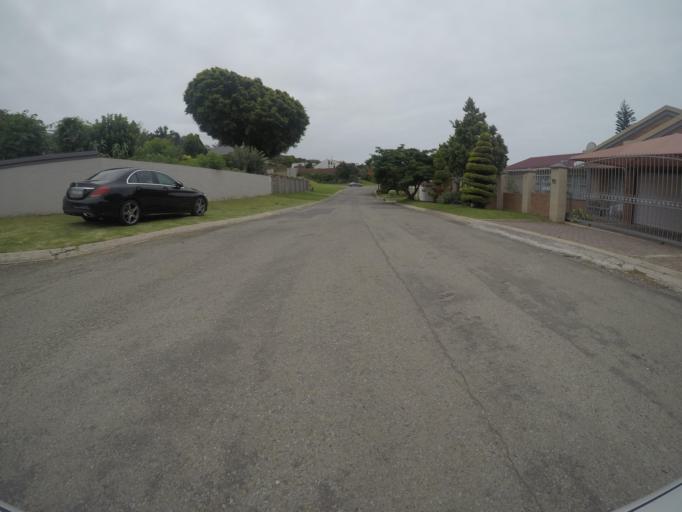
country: ZA
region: Eastern Cape
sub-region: Buffalo City Metropolitan Municipality
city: East London
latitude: -32.9802
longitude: 27.9359
